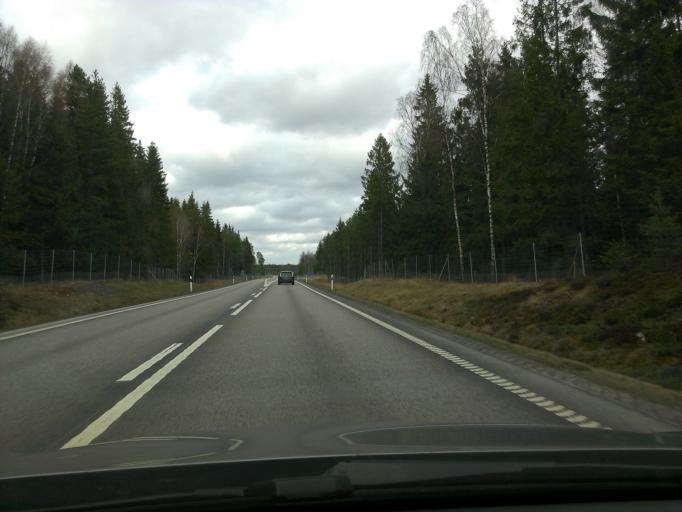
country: SE
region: Kronoberg
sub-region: Almhults Kommun
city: AElmhult
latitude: 56.6448
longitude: 14.2739
